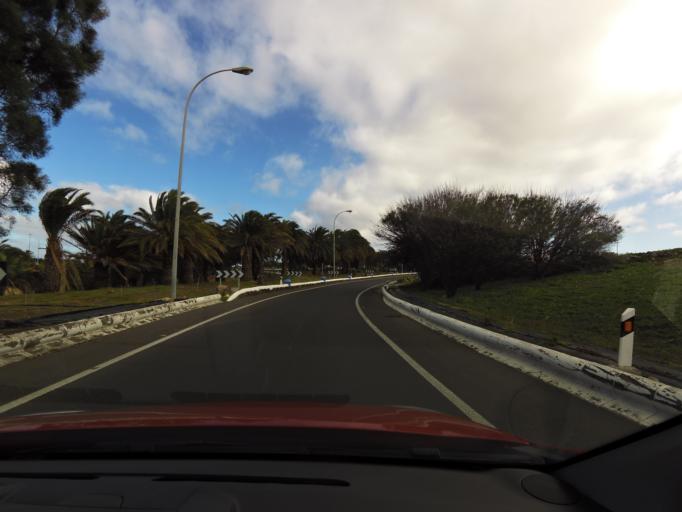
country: ES
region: Canary Islands
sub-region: Provincia de Las Palmas
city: Telde
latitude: 28.0063
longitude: -15.3925
